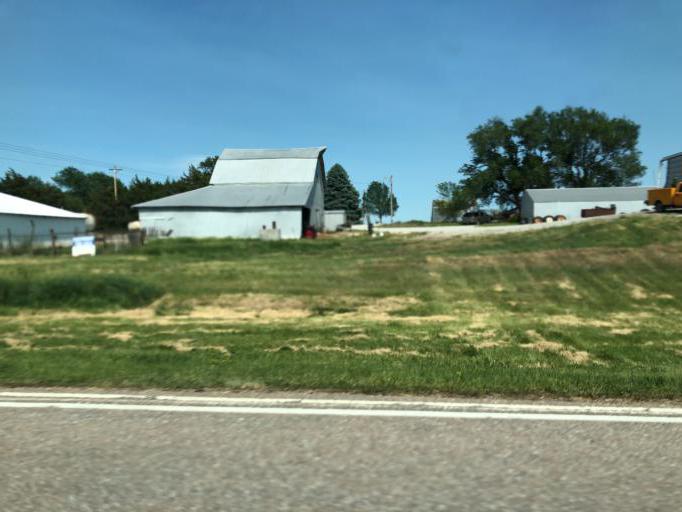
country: US
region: Nebraska
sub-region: York County
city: York
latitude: 40.7412
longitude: -97.6049
